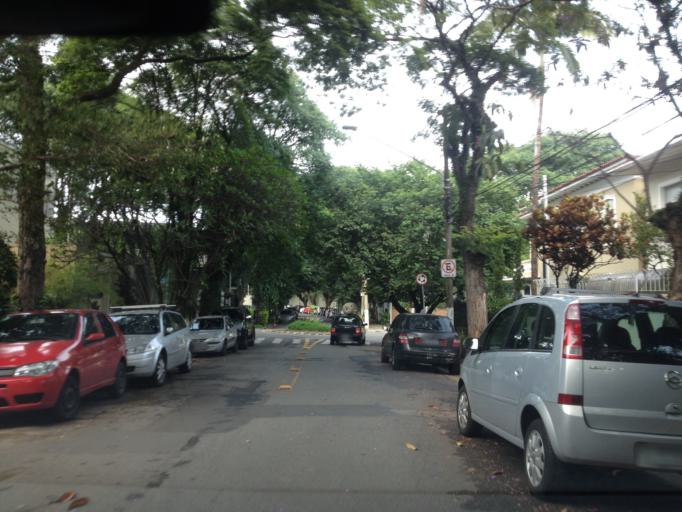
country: BR
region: Sao Paulo
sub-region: Sao Paulo
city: Sao Paulo
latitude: -23.5683
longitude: -46.6806
